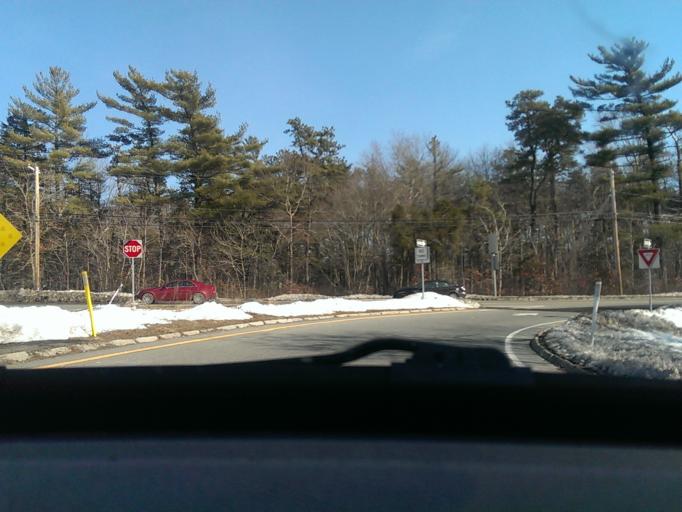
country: US
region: Massachusetts
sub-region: Bristol County
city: Head of Westport
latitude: 41.6554
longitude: -71.0379
